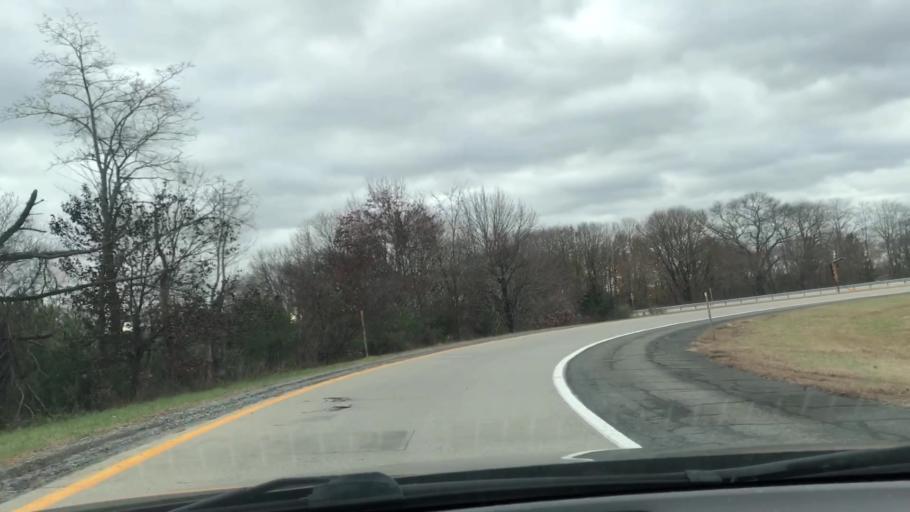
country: US
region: New York
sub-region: Suffolk County
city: Calverton
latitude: 40.9198
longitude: -72.7211
